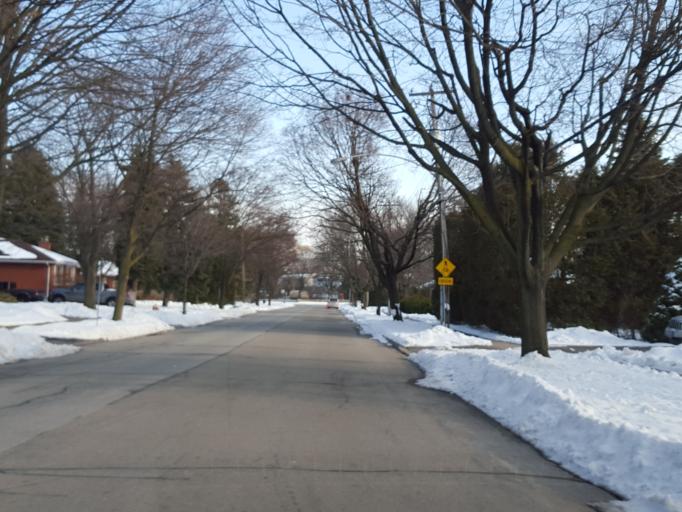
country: CA
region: Ontario
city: Burlington
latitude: 43.3441
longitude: -79.7823
